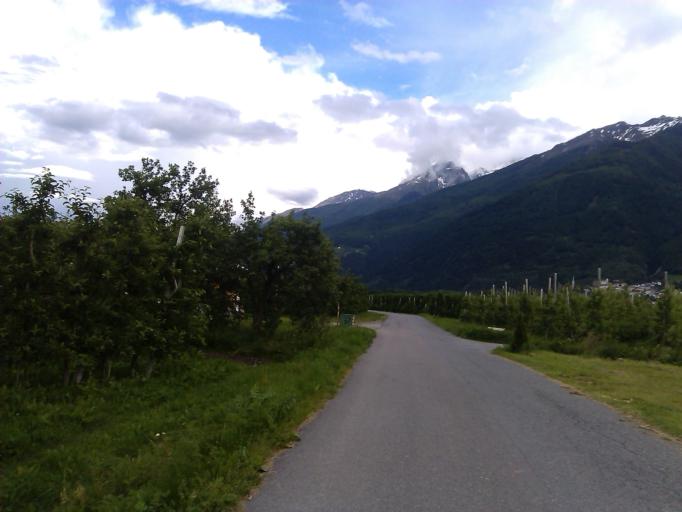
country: IT
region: Trentino-Alto Adige
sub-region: Bolzano
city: Prato Allo Stelvio
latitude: 46.6282
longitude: 10.6176
